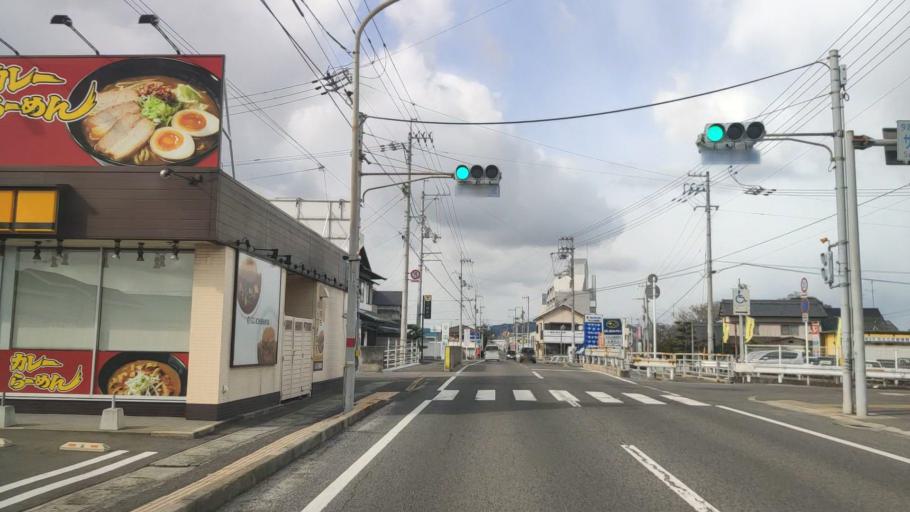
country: JP
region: Ehime
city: Saijo
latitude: 34.0479
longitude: 133.0178
